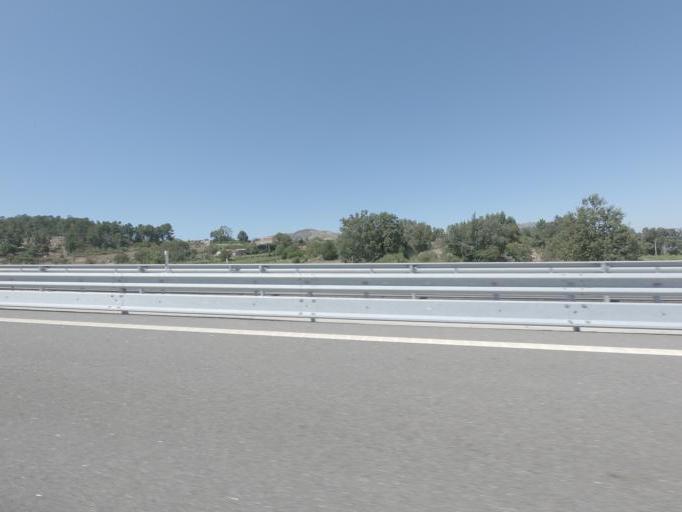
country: PT
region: Vila Real
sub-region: Santa Marta de Penaguiao
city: Santa Marta de Penaguiao
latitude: 41.2649
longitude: -7.8053
